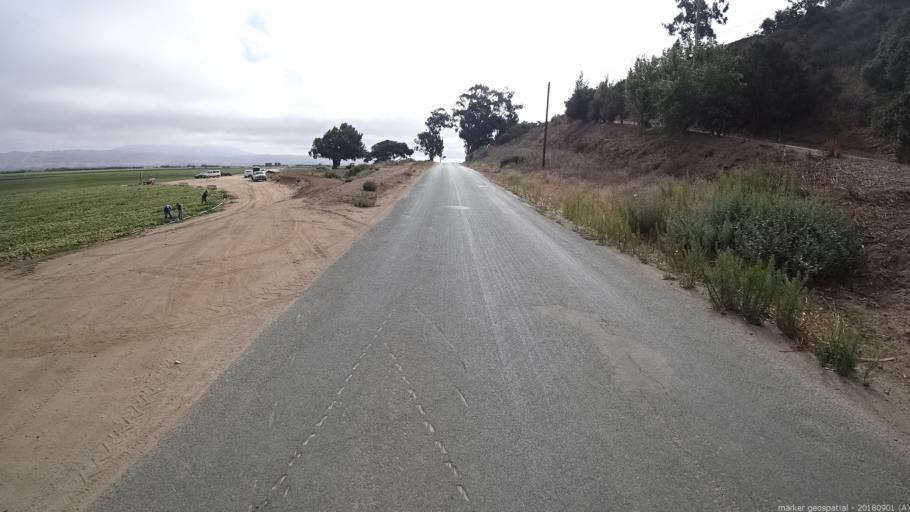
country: US
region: California
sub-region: Monterey County
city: Soledad
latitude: 36.3806
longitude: -121.3457
